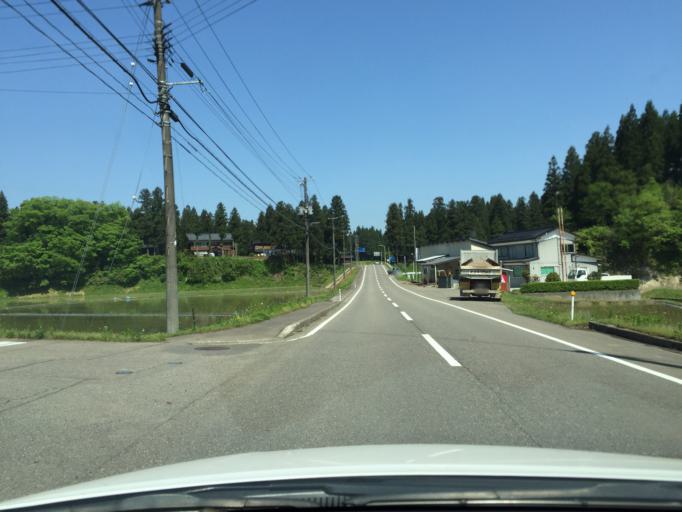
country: JP
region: Niigata
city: Kamo
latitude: 37.5775
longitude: 139.0738
